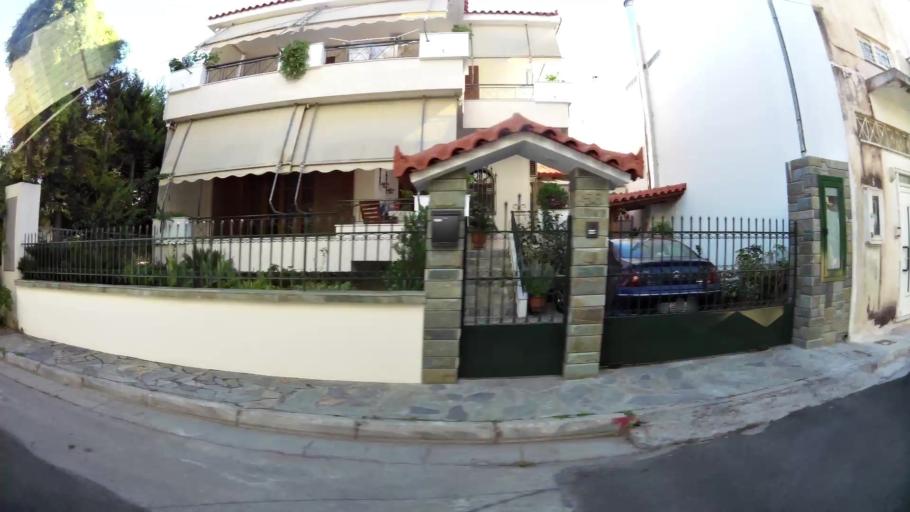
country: GR
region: Attica
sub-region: Nomarchia Anatolikis Attikis
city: Koropi
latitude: 37.9070
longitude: 23.8697
